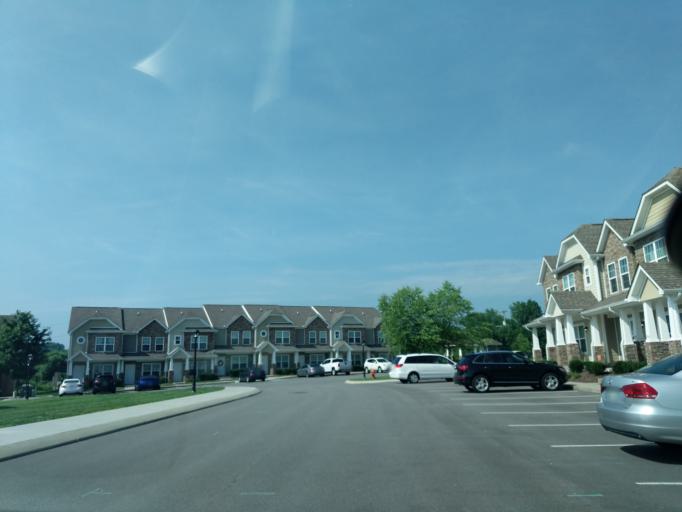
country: US
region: Tennessee
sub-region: Davidson County
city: Goodlettsville
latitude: 36.3006
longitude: -86.7087
